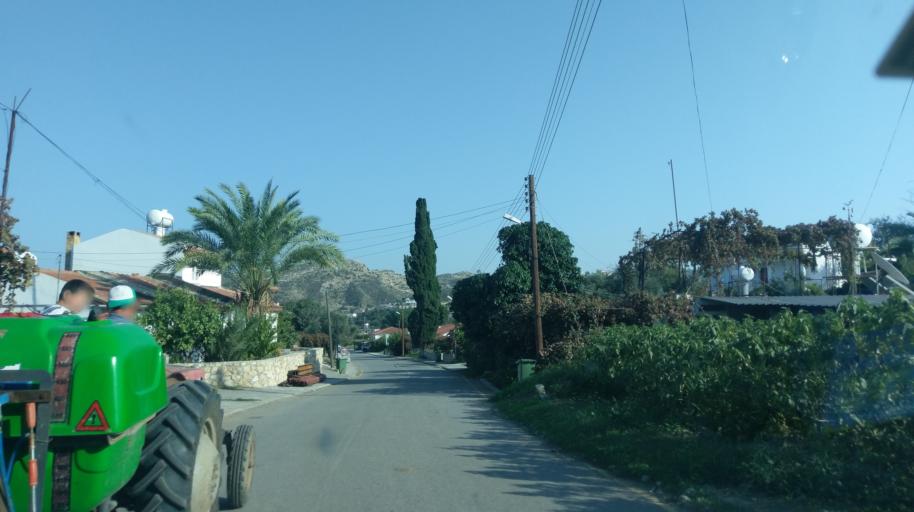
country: CY
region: Lefkosia
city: Kato Pyrgos
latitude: 35.1676
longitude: 32.7352
